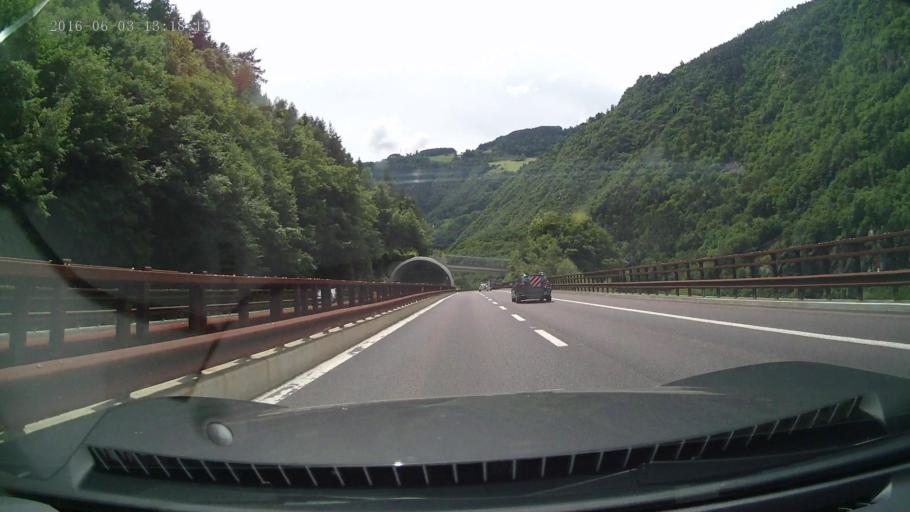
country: IT
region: Trentino-Alto Adige
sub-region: Bolzano
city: Ponte Gardena
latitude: 46.5651
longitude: 11.5181
